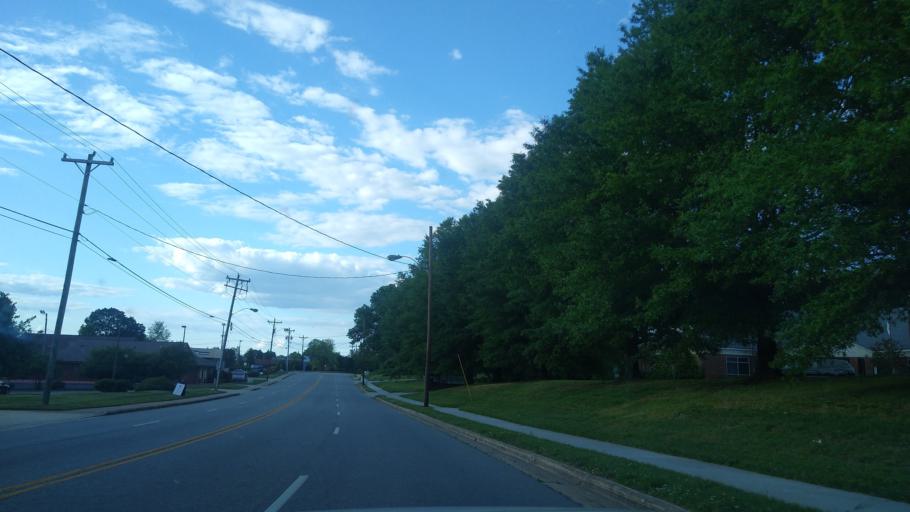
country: US
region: North Carolina
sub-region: Guilford County
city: Greensboro
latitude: 36.0929
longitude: -79.7800
